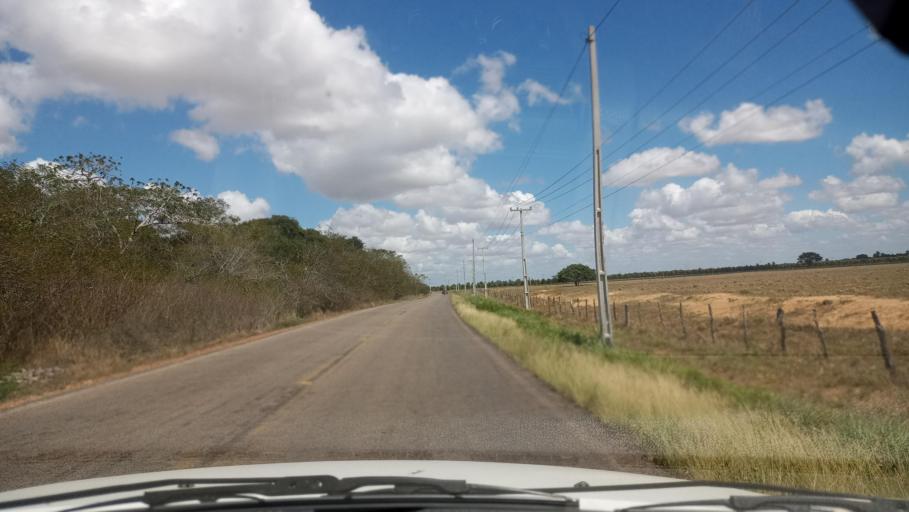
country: BR
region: Rio Grande do Norte
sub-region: Brejinho
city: Brejinho
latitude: -6.0413
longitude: -35.4128
